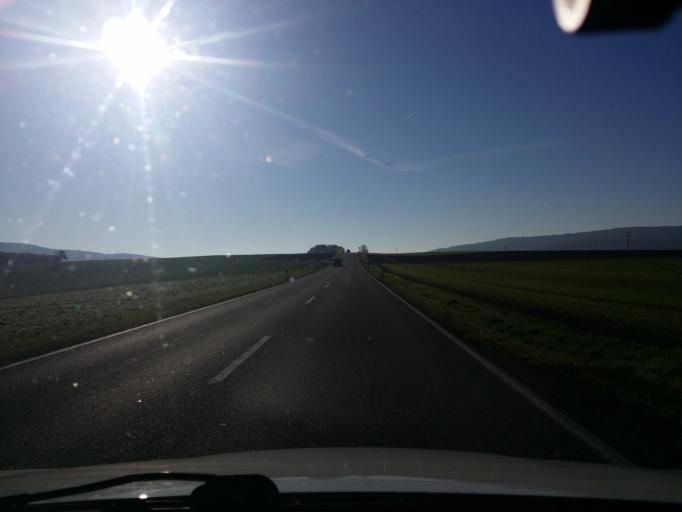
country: DE
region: Hesse
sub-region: Regierungsbezirk Darmstadt
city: Idstein
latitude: 50.2026
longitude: 8.2807
